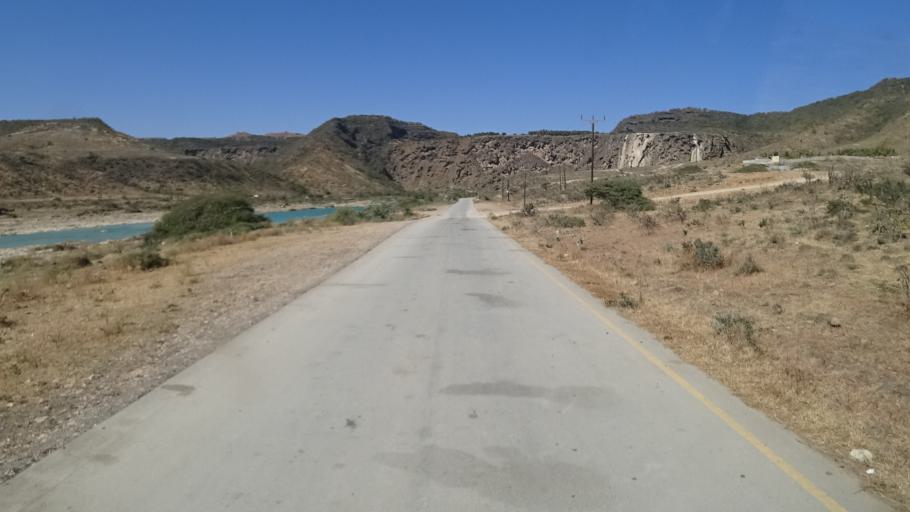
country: OM
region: Zufar
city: Salalah
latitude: 17.0681
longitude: 54.4316
